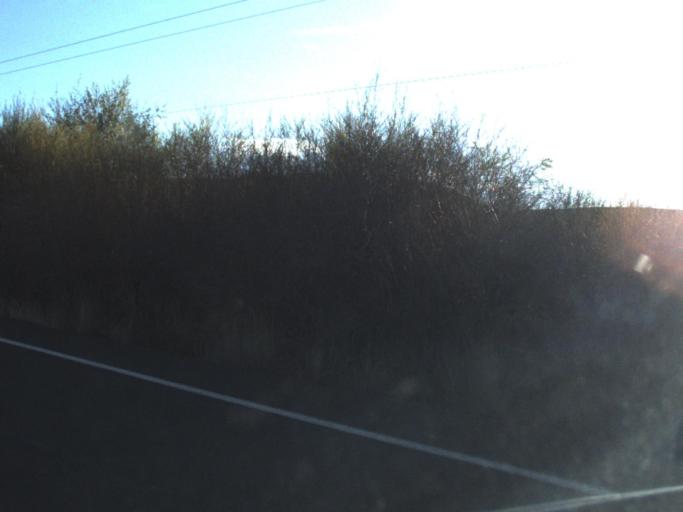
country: US
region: Washington
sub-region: Walla Walla County
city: Waitsburg
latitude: 46.1771
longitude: -118.1385
